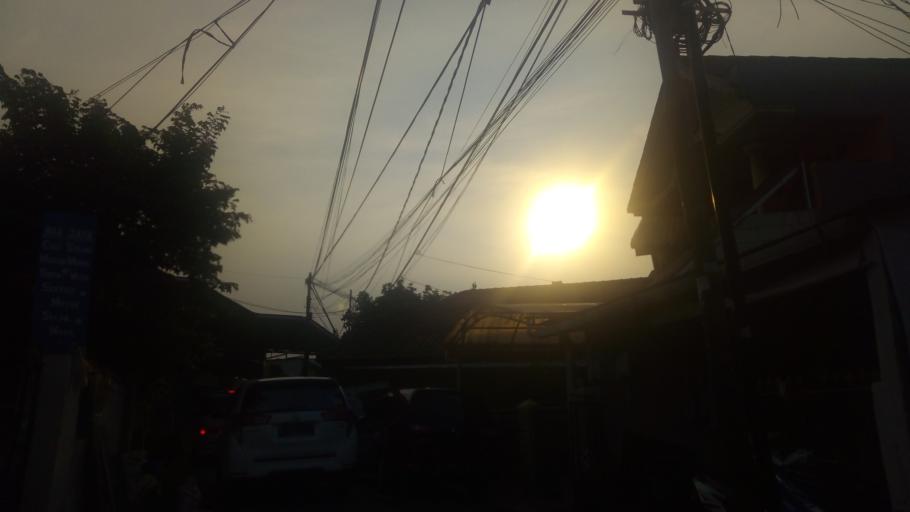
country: ID
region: Jakarta Raya
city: Jakarta
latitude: -6.2057
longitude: 106.8530
